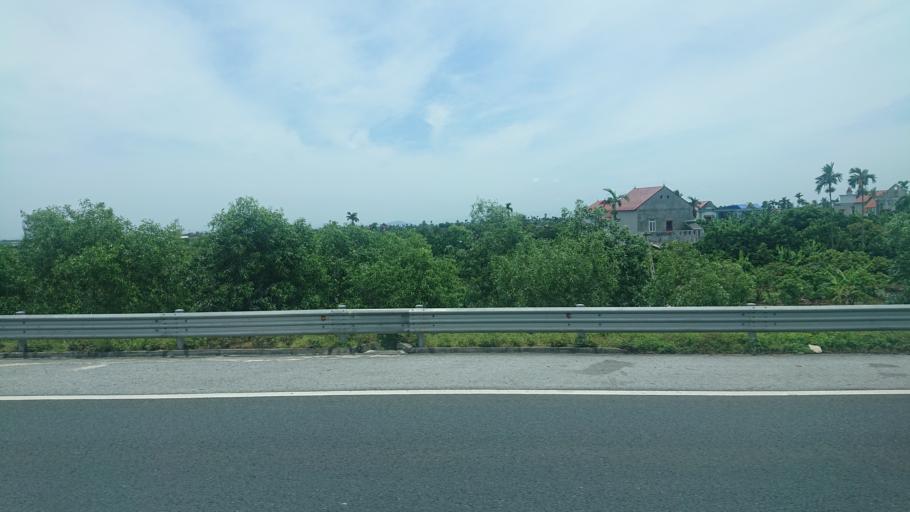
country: VN
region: Hai Duong
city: Tu Ky
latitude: 20.8315
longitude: 106.4463
